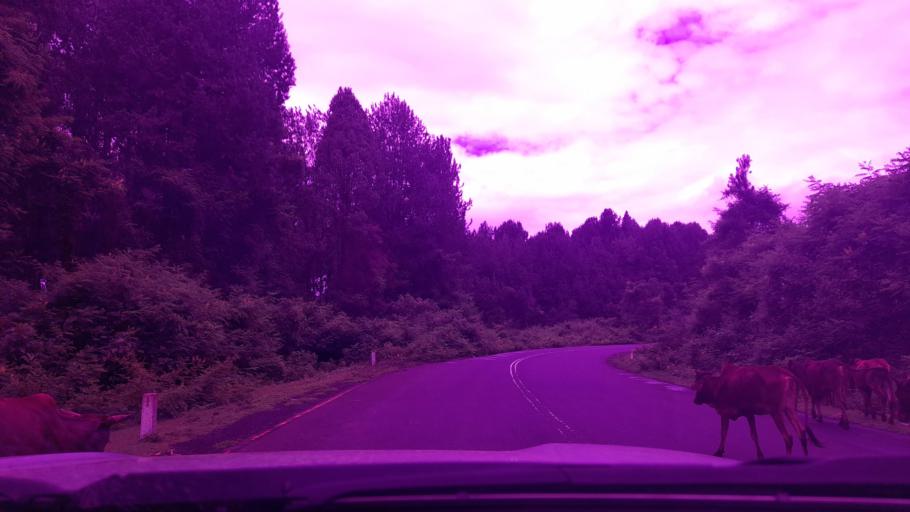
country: ET
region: Oromiya
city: Jima
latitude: 7.5567
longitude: 36.5941
